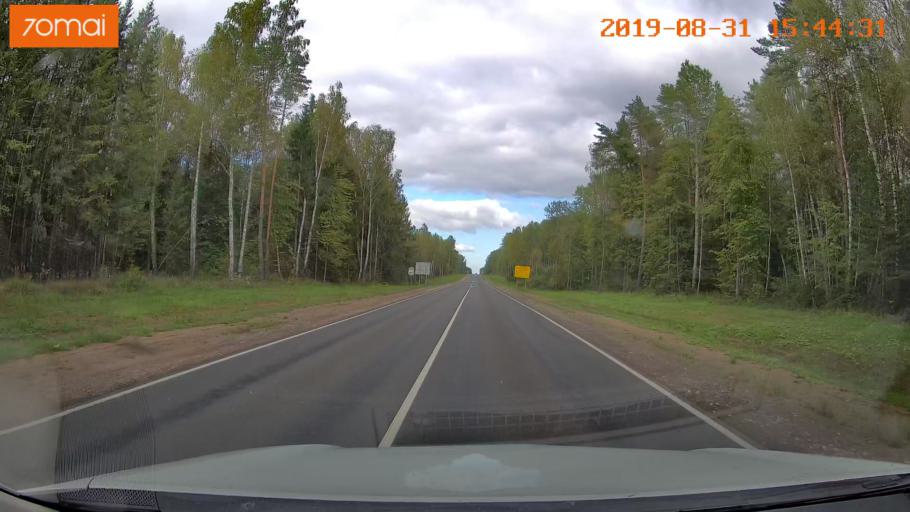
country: RU
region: Kaluga
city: Mosal'sk
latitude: 54.6597
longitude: 34.9351
